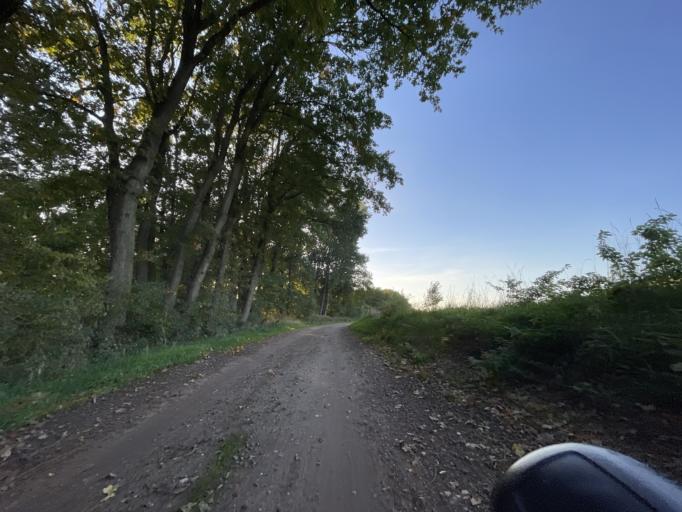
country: DE
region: Lower Saxony
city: Vastorf
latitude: 53.2034
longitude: 10.5336
